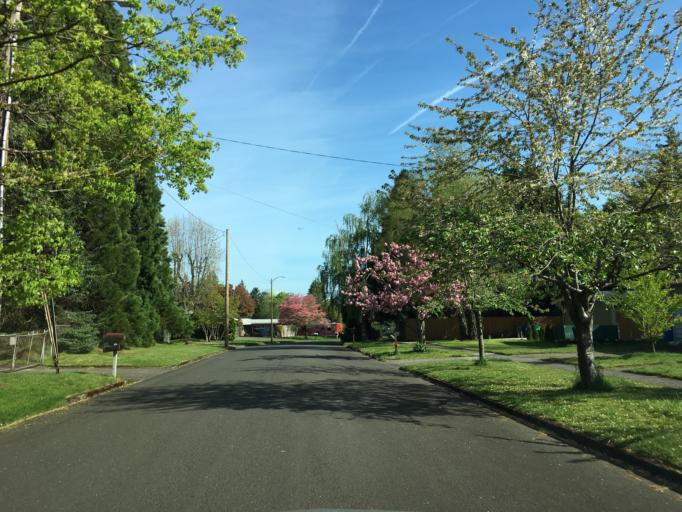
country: US
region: Oregon
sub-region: Multnomah County
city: Lents
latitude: 45.5398
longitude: -122.5244
